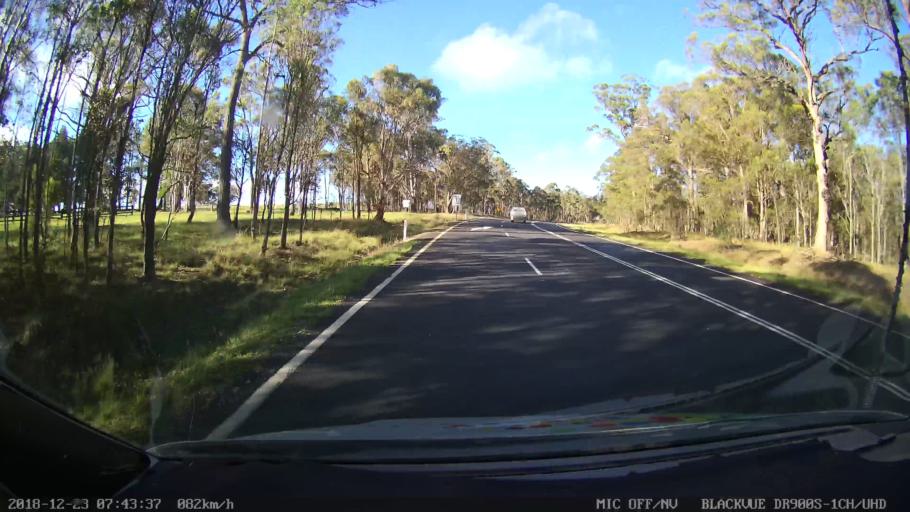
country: AU
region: New South Wales
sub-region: Armidale Dumaresq
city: Enmore
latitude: -30.5235
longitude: 151.9620
